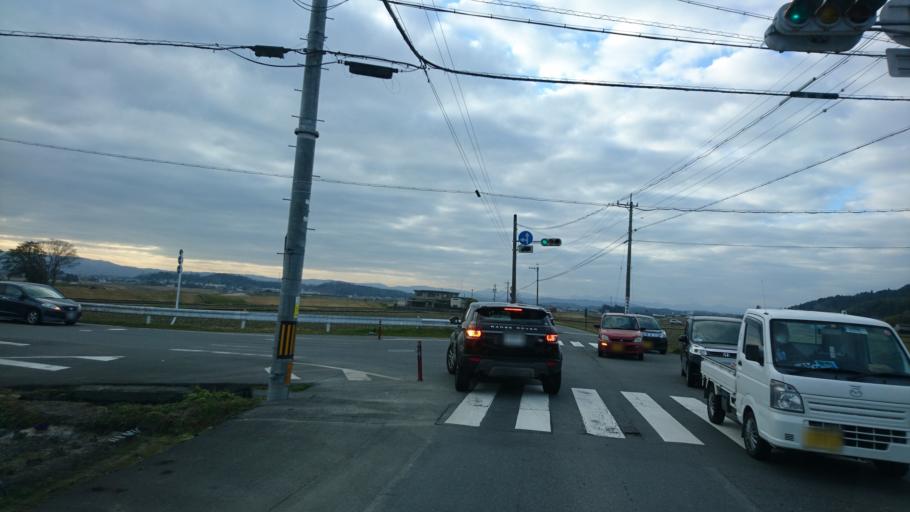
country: JP
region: Mie
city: Ueno-ebisumachi
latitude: 34.7667
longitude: 136.1080
